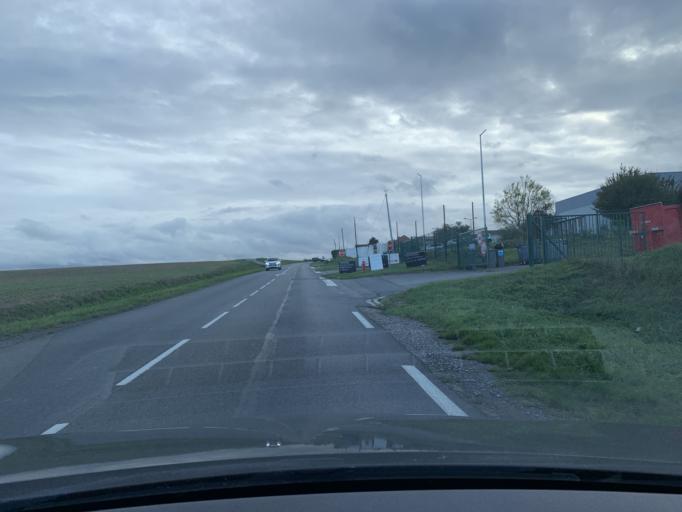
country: FR
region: Nord-Pas-de-Calais
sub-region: Departement du Nord
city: Proville
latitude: 50.1456
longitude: 3.2143
